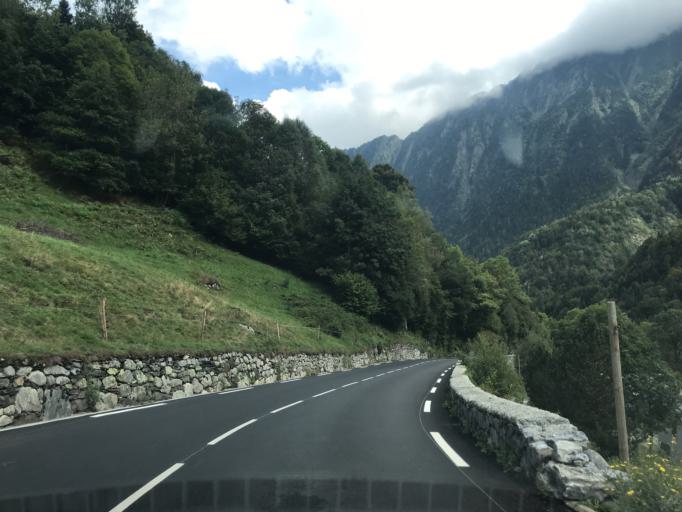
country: FR
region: Midi-Pyrenees
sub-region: Departement des Hautes-Pyrenees
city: Saint-Lary-Soulan
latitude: 42.7882
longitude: 0.2393
